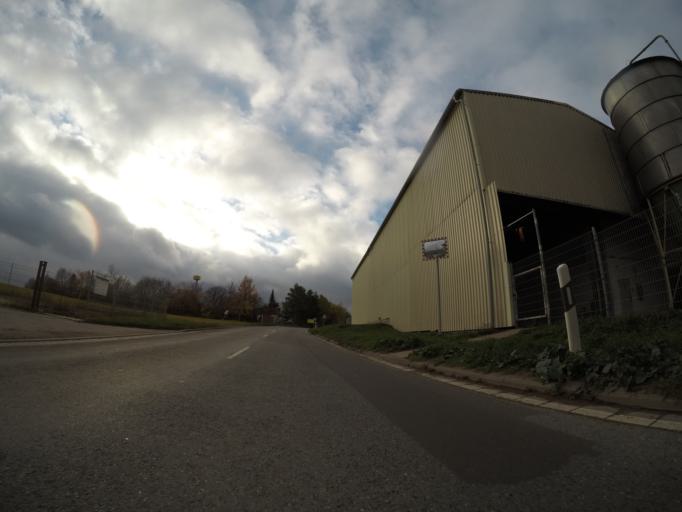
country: DE
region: Thuringia
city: Heyersdorf
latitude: 50.8710
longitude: 12.3579
